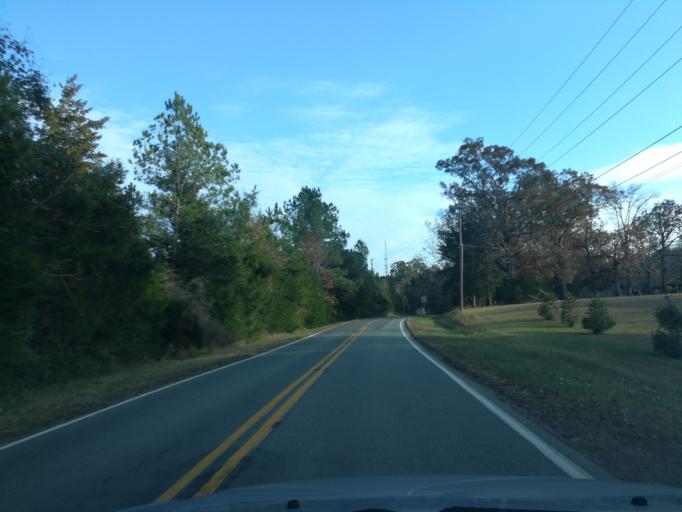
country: US
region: North Carolina
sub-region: Orange County
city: Chapel Hill
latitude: 35.9666
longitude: -79.0035
